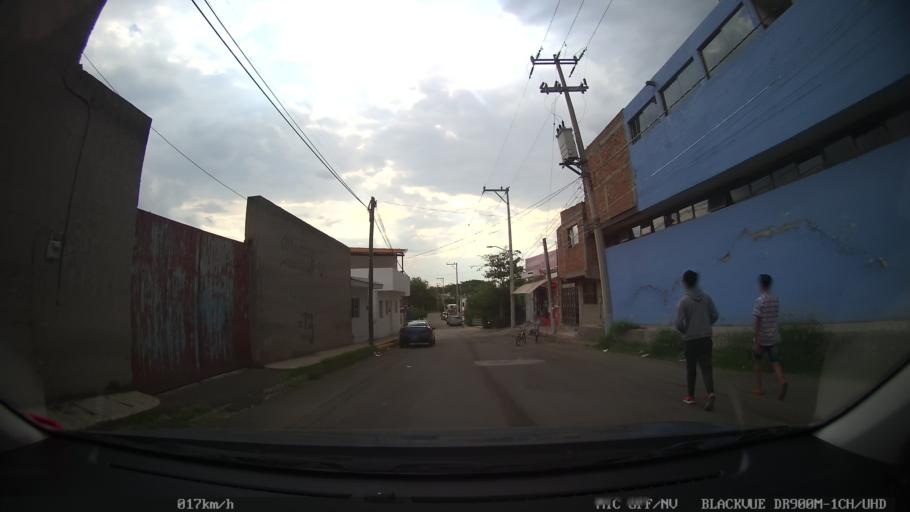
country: MX
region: Jalisco
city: Tlaquepaque
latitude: 20.6235
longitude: -103.2682
